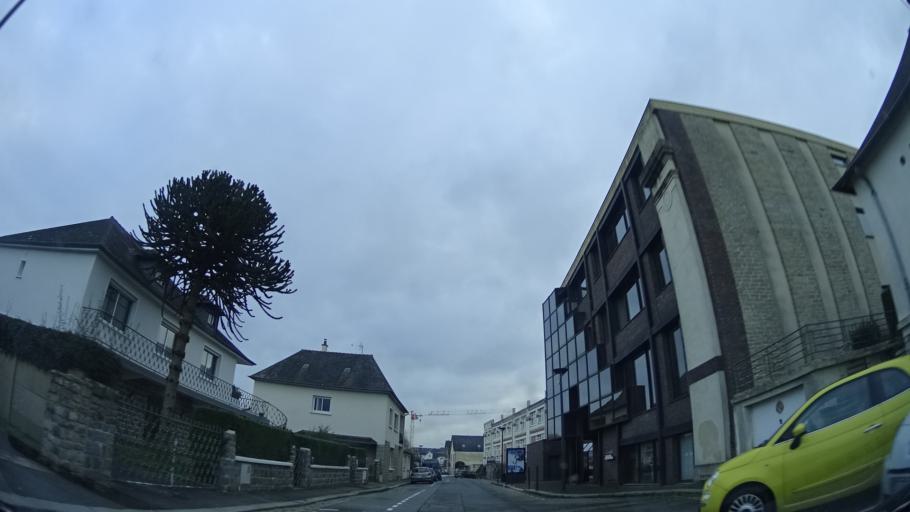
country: FR
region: Brittany
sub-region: Departement d'Ille-et-Vilaine
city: Vitre
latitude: 48.1218
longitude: -1.2162
